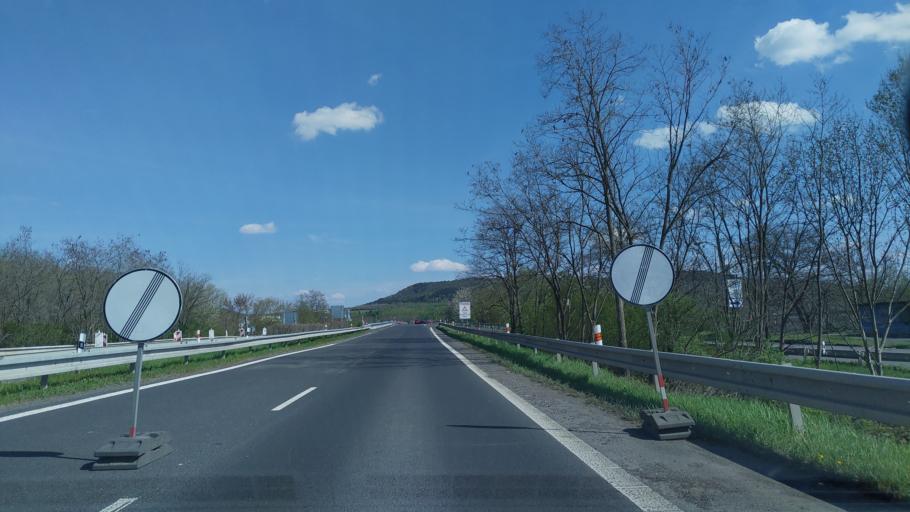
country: CZ
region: Ustecky
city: Horni Jiretin
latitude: 50.5266
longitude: 13.5782
